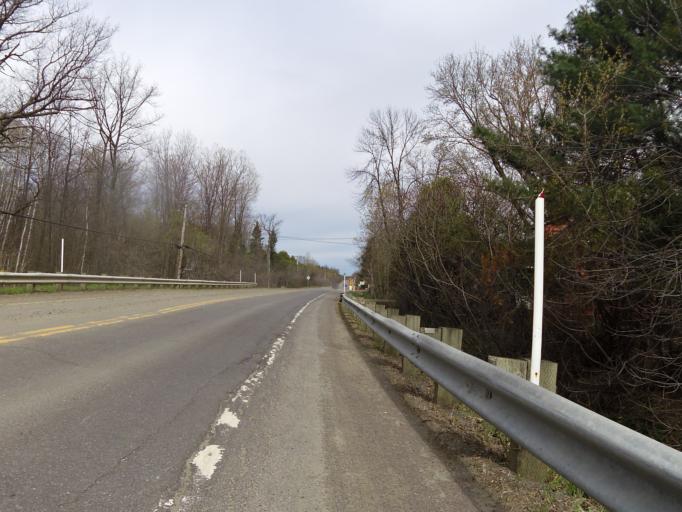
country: CA
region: Quebec
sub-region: Laurentides
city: Oka
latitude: 45.4675
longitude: -74.1148
